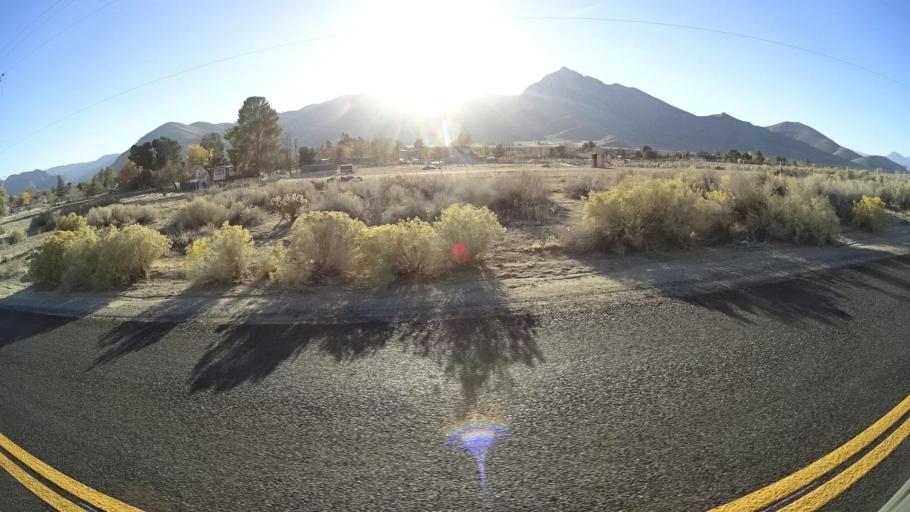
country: US
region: California
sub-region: Kern County
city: Weldon
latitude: 35.6357
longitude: -118.2453
